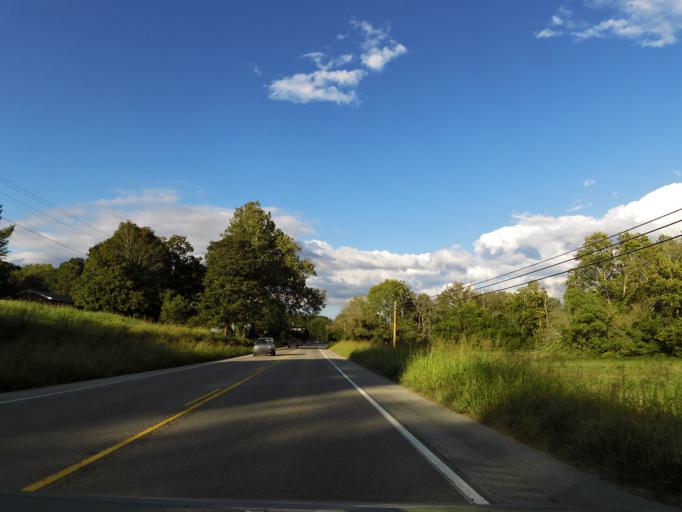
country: US
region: Tennessee
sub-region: Grainger County
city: Rutledge
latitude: 36.2601
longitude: -83.5714
